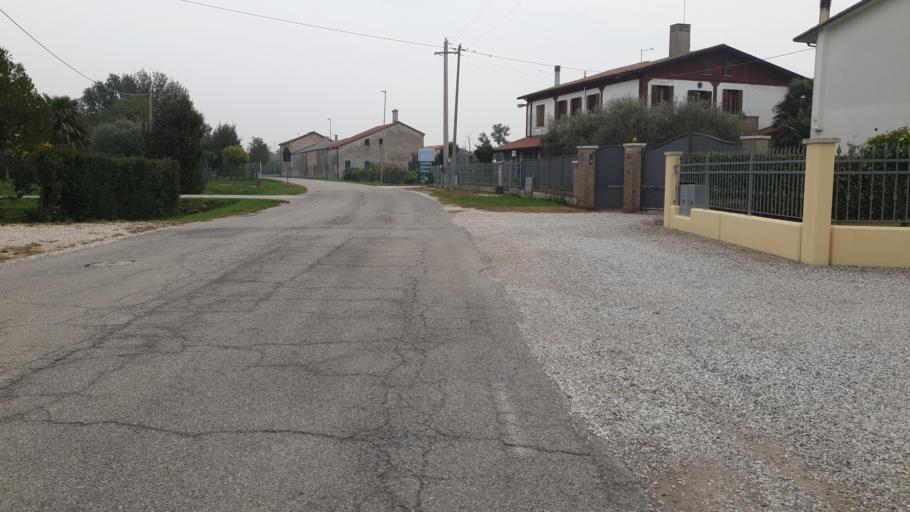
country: IT
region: Veneto
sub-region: Provincia di Padova
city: Casalserugo
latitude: 45.2985
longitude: 11.9117
